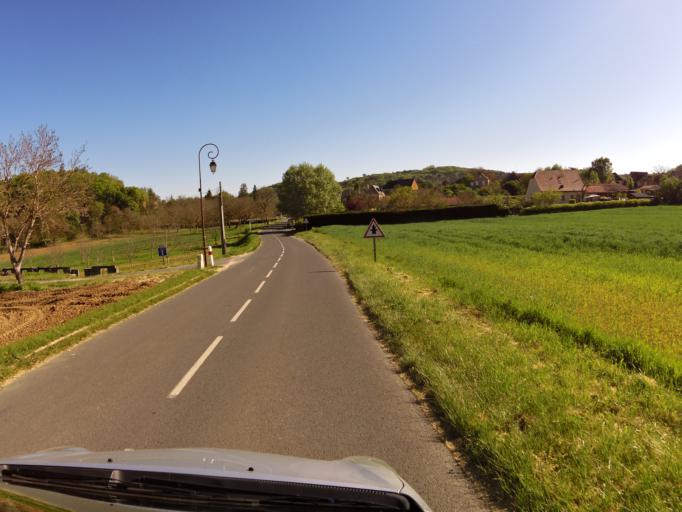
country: FR
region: Aquitaine
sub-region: Departement de la Dordogne
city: Carsac-Aillac
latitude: 44.8290
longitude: 1.3066
